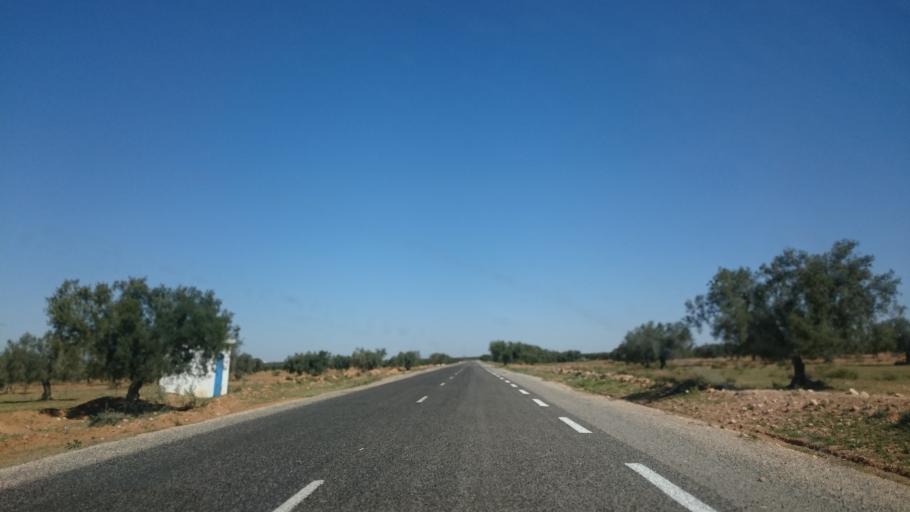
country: TN
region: Safaqis
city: Sfax
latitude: 34.8296
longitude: 10.4660
